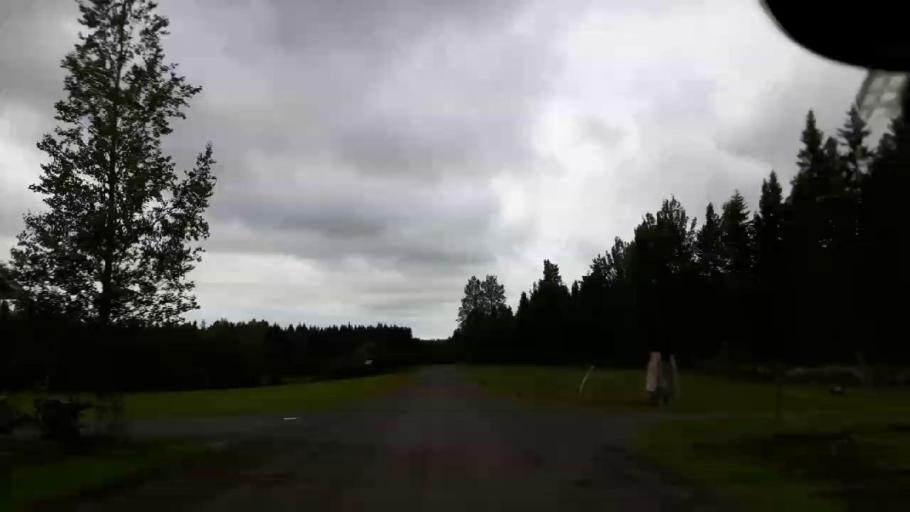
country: SE
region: Jaemtland
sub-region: OEstersunds Kommun
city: Ostersund
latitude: 63.0212
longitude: 14.5855
